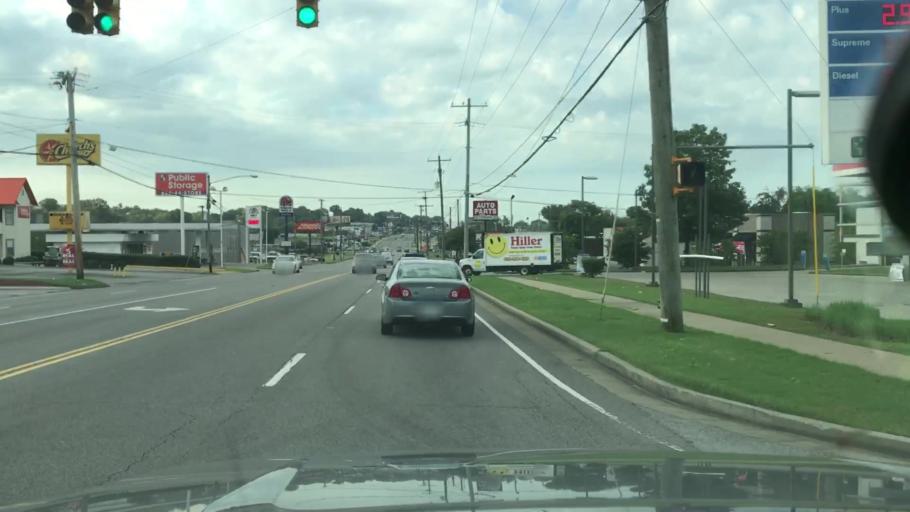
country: US
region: Tennessee
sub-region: Davidson County
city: Nashville
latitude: 36.2330
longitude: -86.7587
